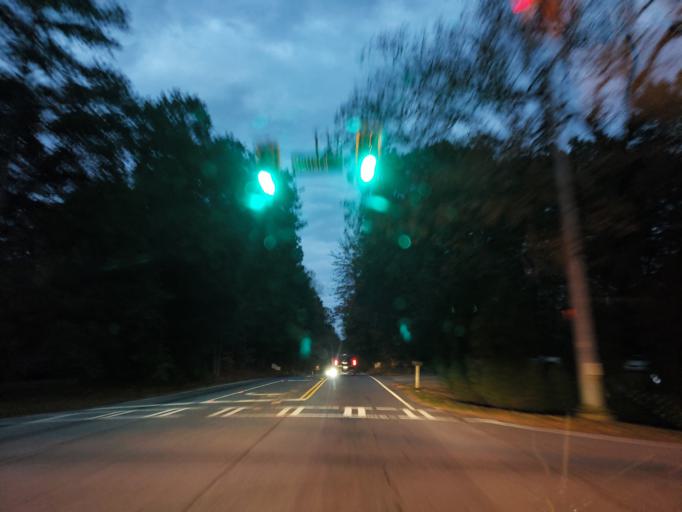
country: US
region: Georgia
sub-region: Cobb County
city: Powder Springs
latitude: 33.9147
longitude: -84.6889
